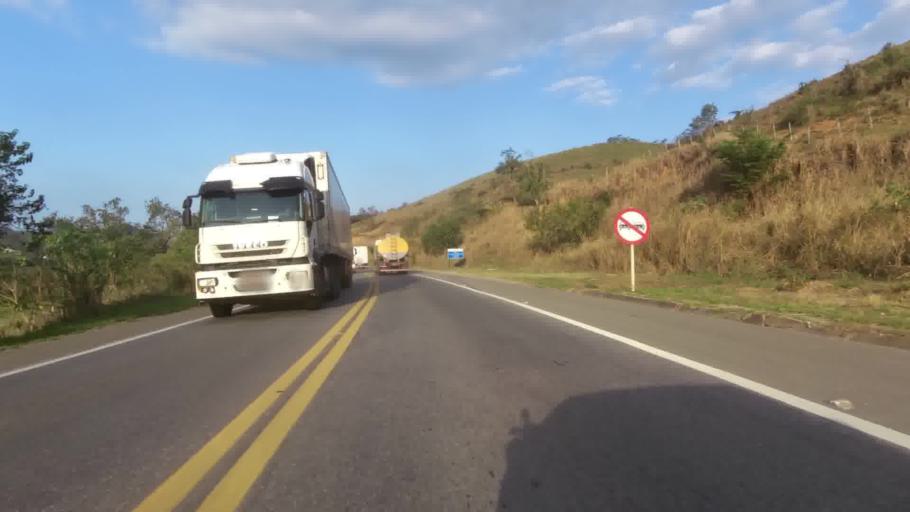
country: BR
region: Espirito Santo
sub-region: Rio Novo Do Sul
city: Rio Novo do Sul
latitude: -20.8816
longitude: -40.9742
